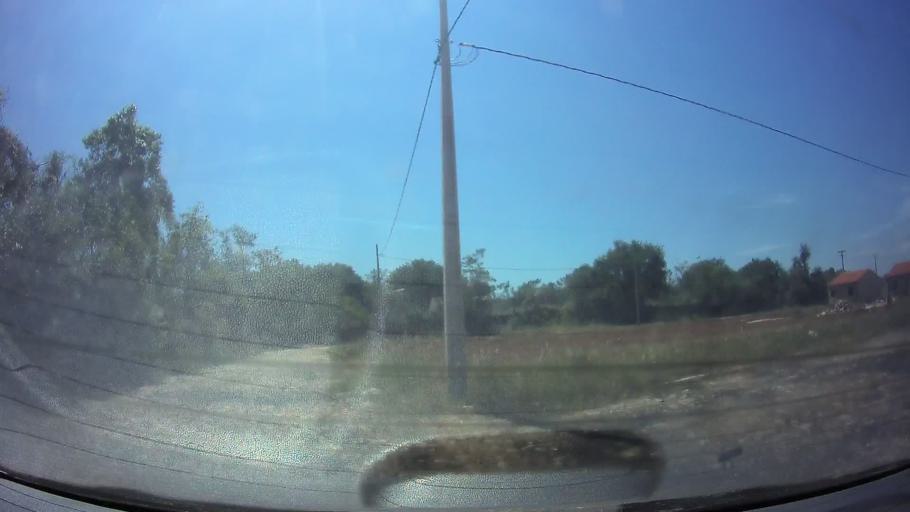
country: PY
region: Central
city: Limpio
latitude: -25.2279
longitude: -57.4359
